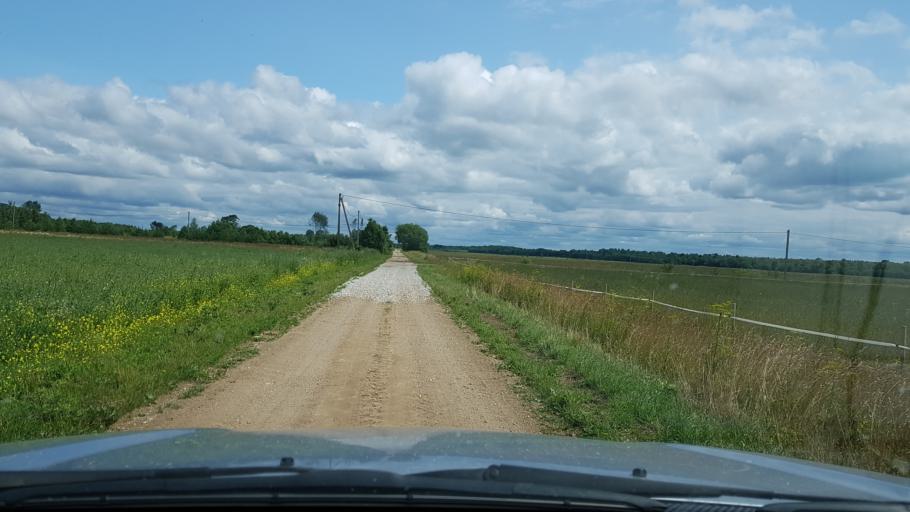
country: EE
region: Ida-Virumaa
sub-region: Sillamaee linn
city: Sillamae
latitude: 59.3679
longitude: 27.8517
